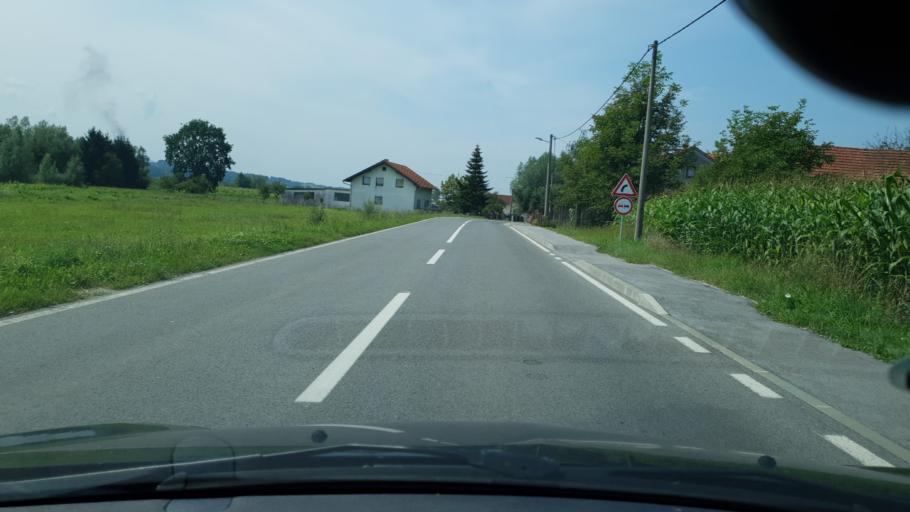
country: HR
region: Krapinsko-Zagorska
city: Bedekovcina
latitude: 46.0306
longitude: 15.9671
